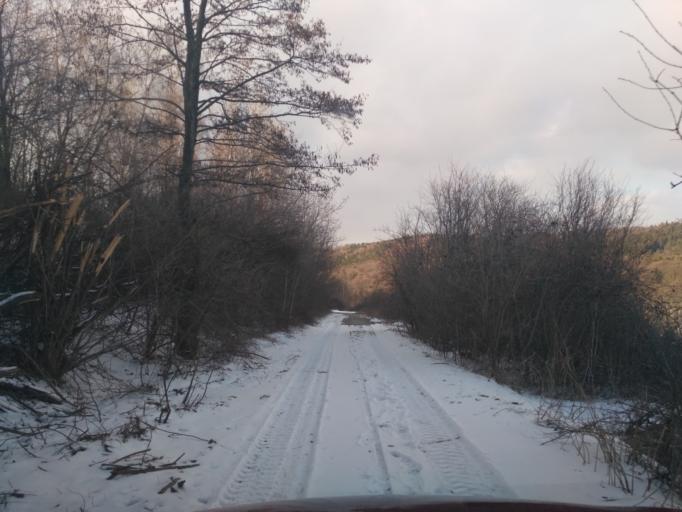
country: SK
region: Kosicky
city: Kosice
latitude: 48.7370
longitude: 21.1503
